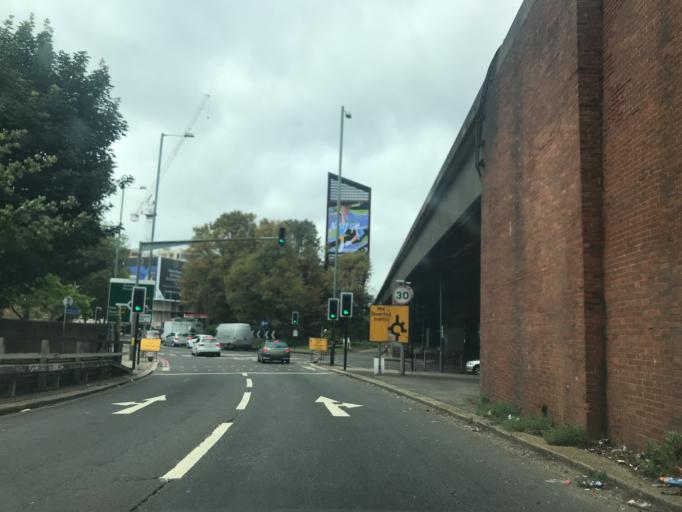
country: GB
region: England
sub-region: Greater London
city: Acton
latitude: 51.4908
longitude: -0.2809
